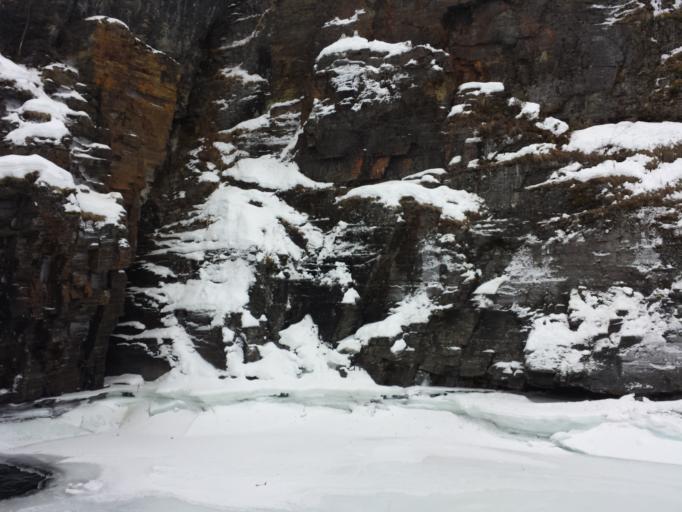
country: NO
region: Troms
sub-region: Bardu
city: Setermoen
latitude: 68.3597
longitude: 18.7761
